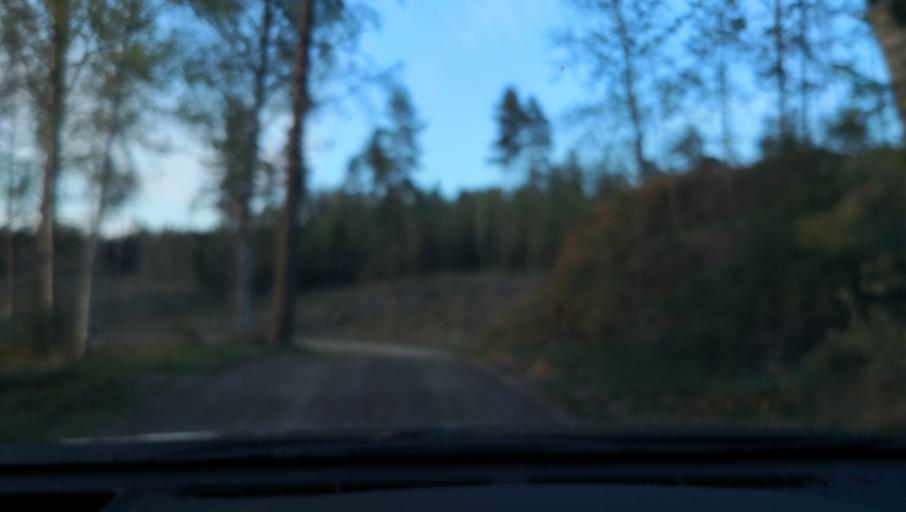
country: SE
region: OErebro
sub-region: Askersunds Kommun
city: Askersund
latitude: 58.9689
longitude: 14.9515
